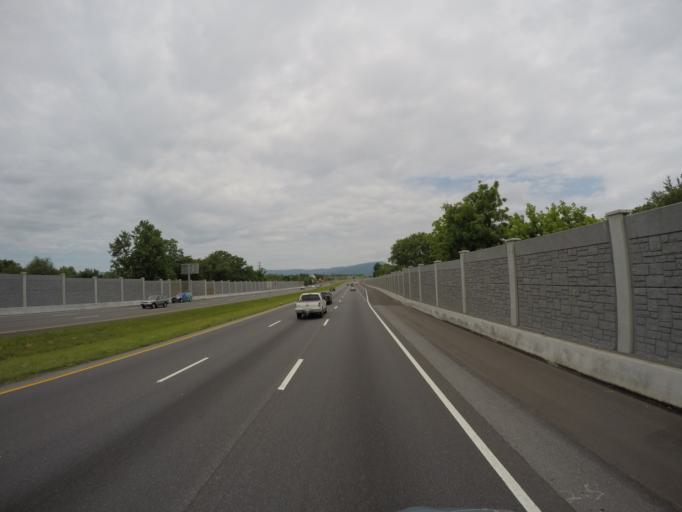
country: US
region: Virginia
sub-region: City of Roanoke
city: Roanoke
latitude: 37.2950
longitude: -79.9494
